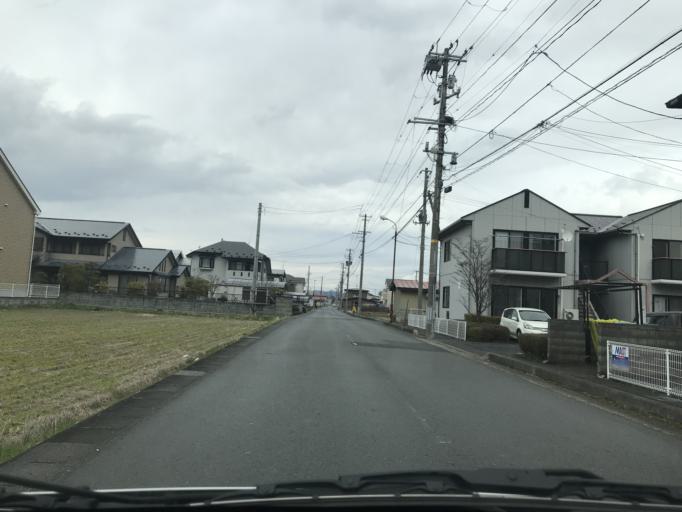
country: JP
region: Iwate
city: Mizusawa
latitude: 39.1496
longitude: 141.1378
